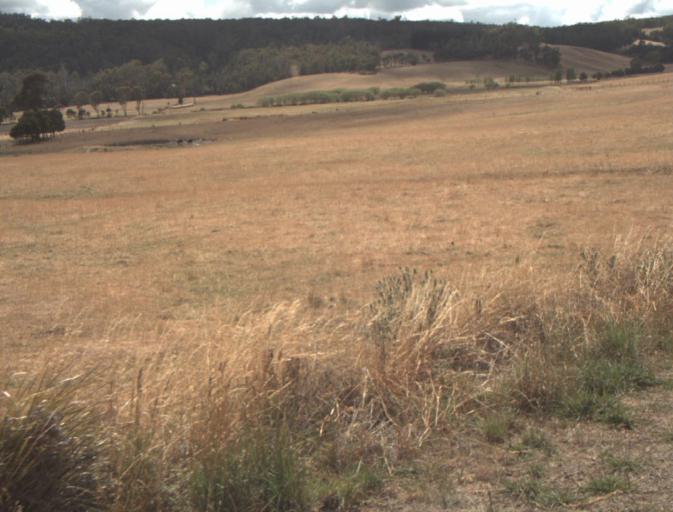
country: AU
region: Tasmania
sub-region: Launceston
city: Mayfield
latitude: -41.2195
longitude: 147.1499
